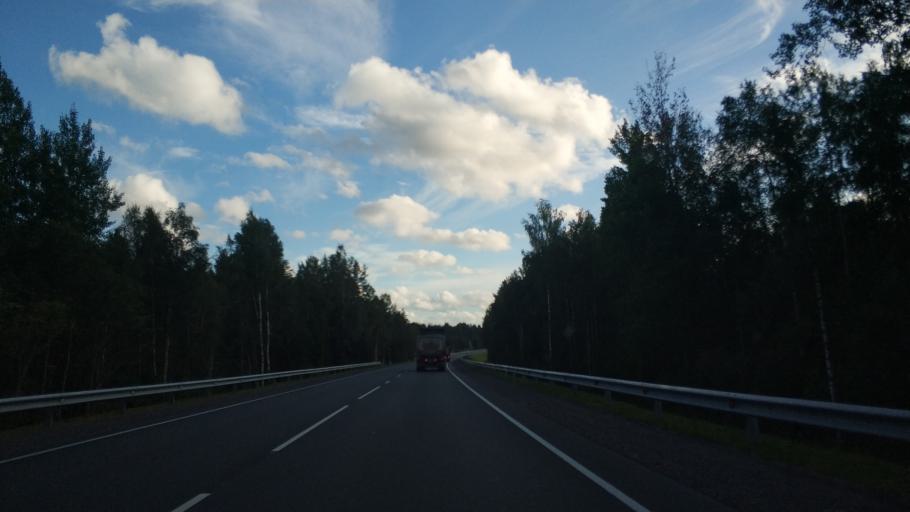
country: RU
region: Leningrad
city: Priozersk
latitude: 60.8642
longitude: 30.1590
